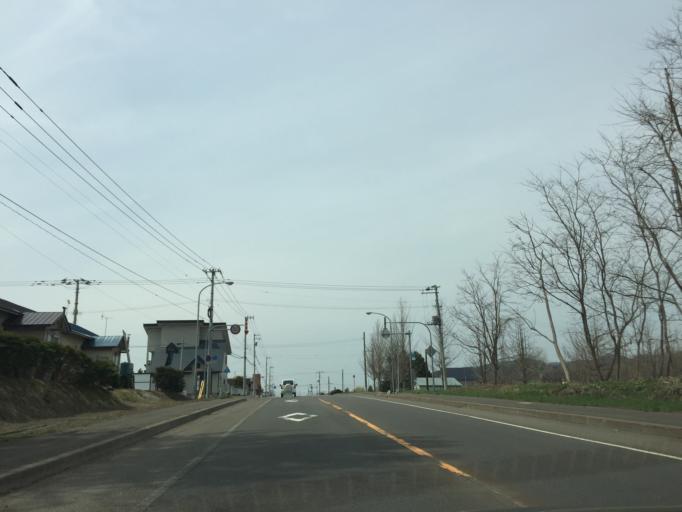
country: JP
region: Hokkaido
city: Akabira
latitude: 43.5367
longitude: 142.0951
